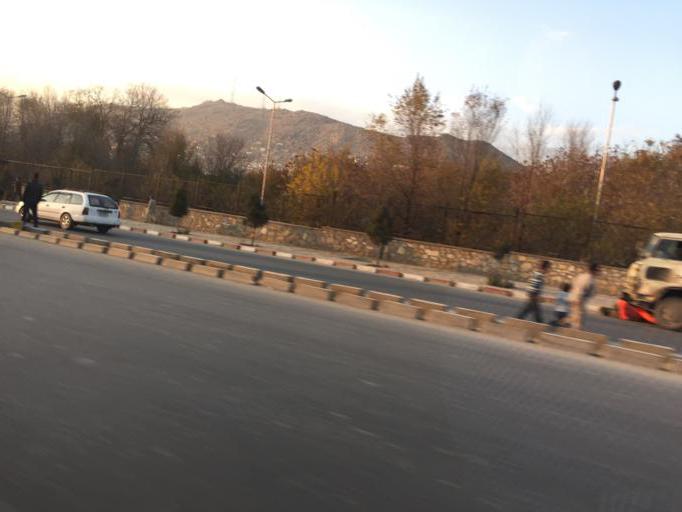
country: AF
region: Kabul
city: Kabul
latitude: 34.5335
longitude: 69.1251
